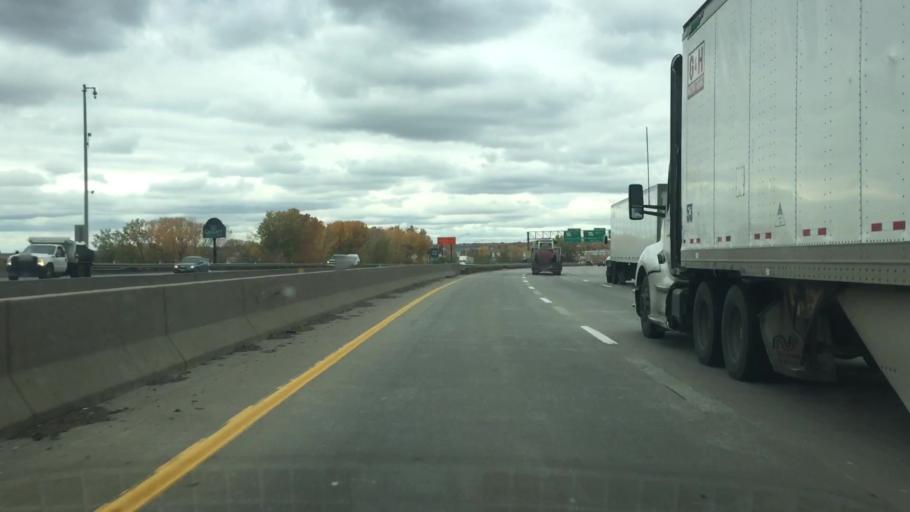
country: US
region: Missouri
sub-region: Jackson County
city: Sugar Creek
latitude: 39.1258
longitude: -94.4967
